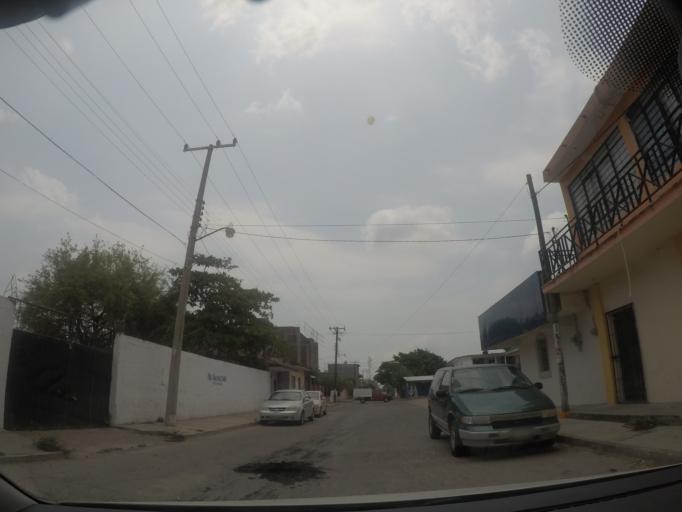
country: MX
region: Oaxaca
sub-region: El Espinal
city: El Espinal
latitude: 16.4886
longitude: -95.0441
